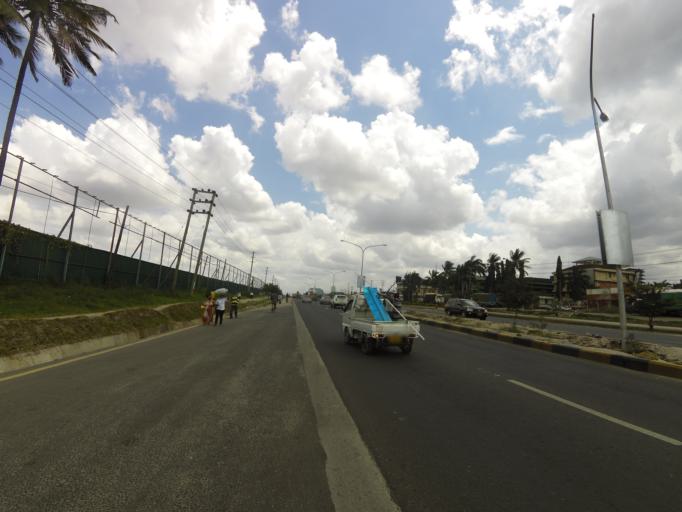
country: TZ
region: Dar es Salaam
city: Dar es Salaam
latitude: -6.8584
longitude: 39.2168
